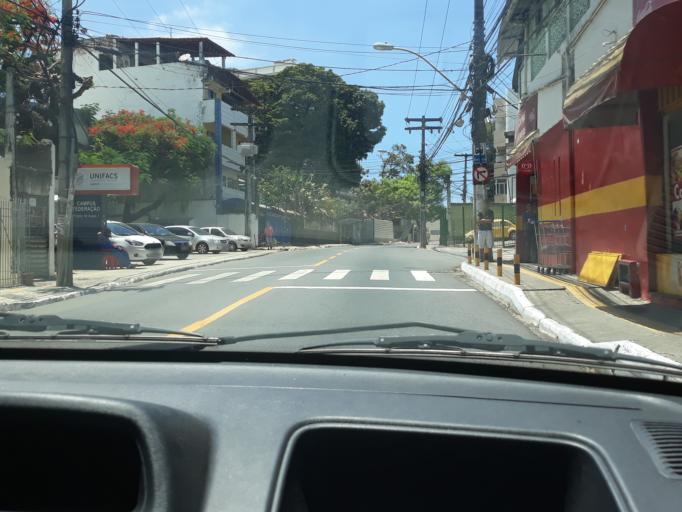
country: BR
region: Bahia
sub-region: Salvador
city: Salvador
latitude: -13.0001
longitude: -38.5031
